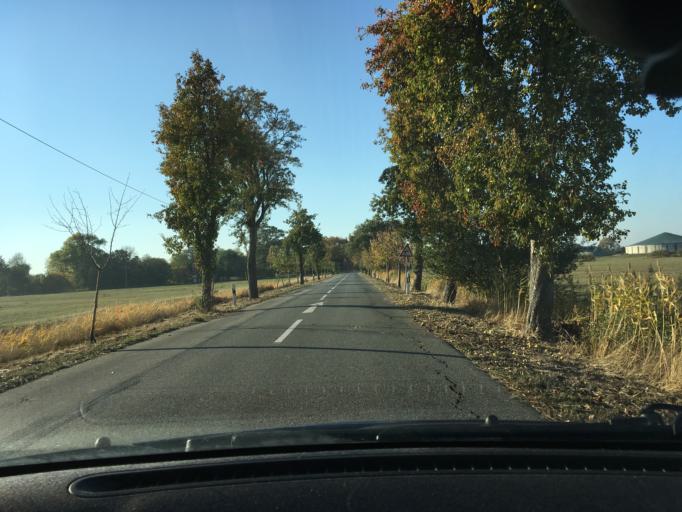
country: DE
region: Lower Saxony
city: Hitzacker
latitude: 53.1541
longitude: 11.0807
